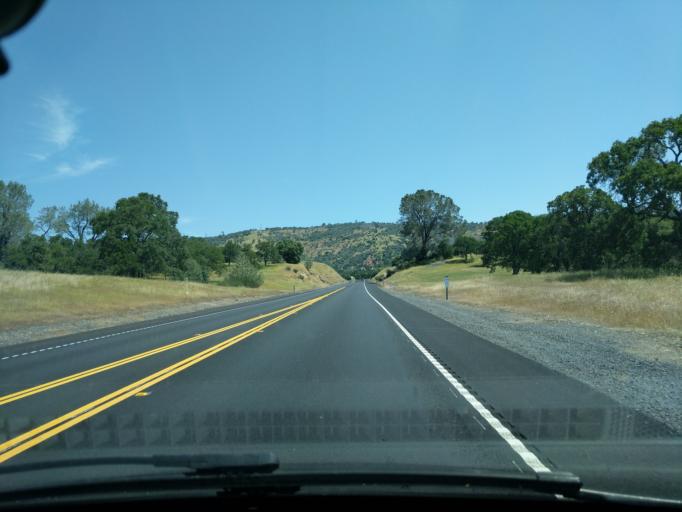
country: US
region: California
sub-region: Calaveras County
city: Copperopolis
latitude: 37.9730
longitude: -120.6557
